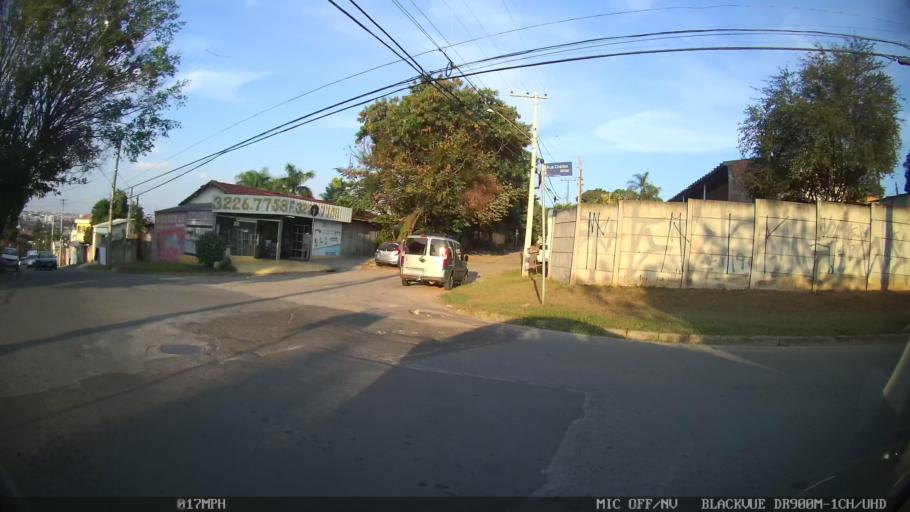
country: BR
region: Sao Paulo
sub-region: Campinas
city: Campinas
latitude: -22.9644
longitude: -47.1297
